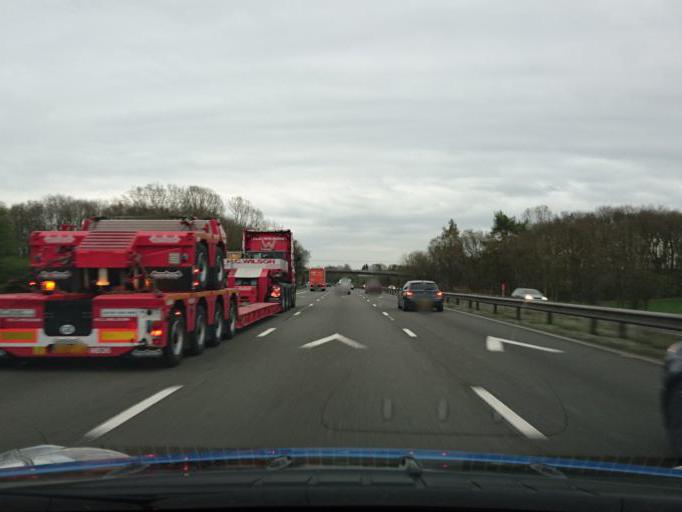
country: GB
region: England
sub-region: Staffordshire
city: Barlaston
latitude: 52.9218
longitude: -2.2055
